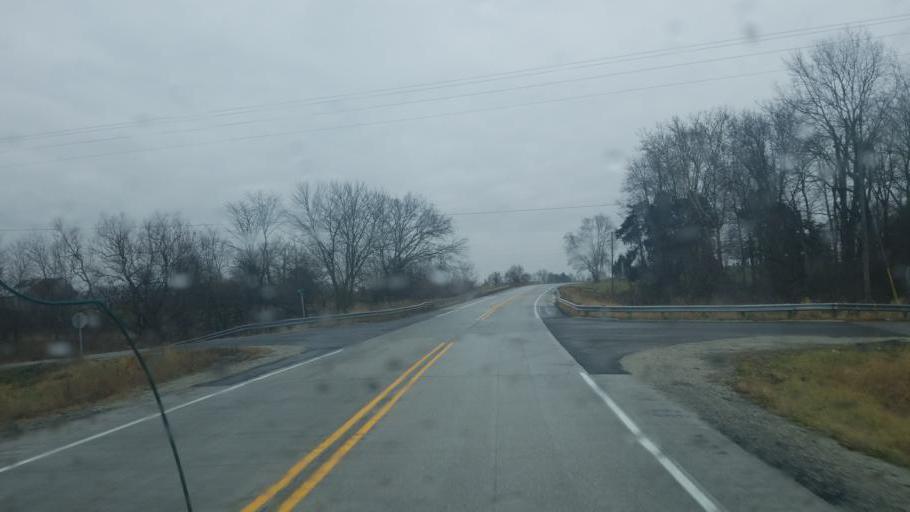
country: US
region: Indiana
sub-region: Shelby County
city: Geneva
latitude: 39.4246
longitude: -85.7511
